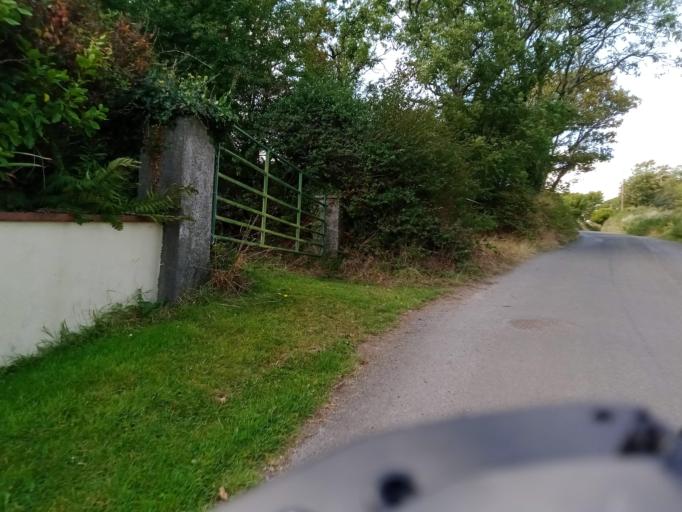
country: IE
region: Munster
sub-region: Waterford
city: Dungarvan
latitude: 52.1272
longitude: -7.4481
